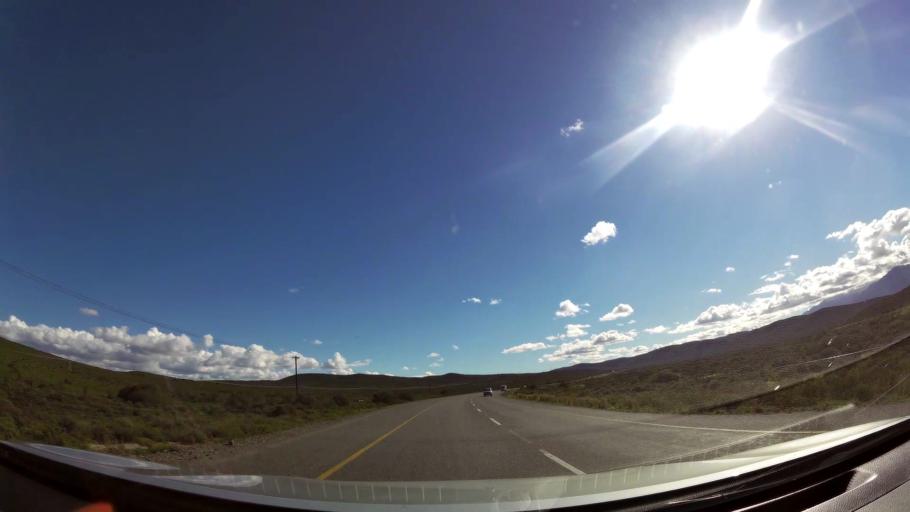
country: ZA
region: Western Cape
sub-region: Cape Winelands District Municipality
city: Worcester
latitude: -33.7504
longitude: 19.7100
